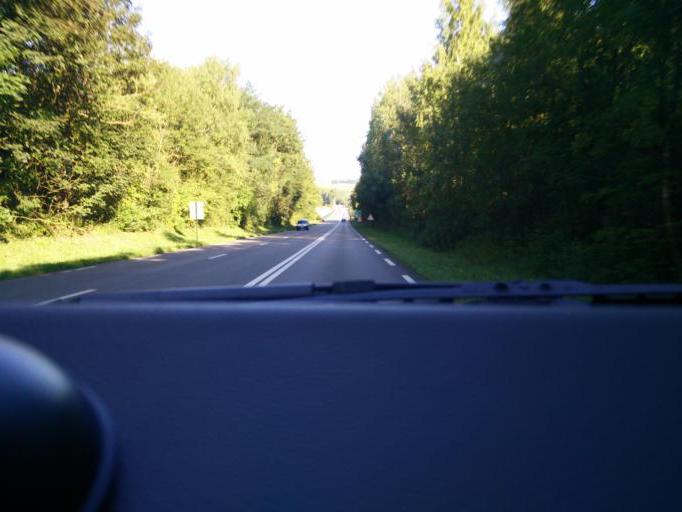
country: FR
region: Nord-Pas-de-Calais
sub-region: Departement du Pas-de-Calais
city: Houdain
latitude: 50.4686
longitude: 2.5285
